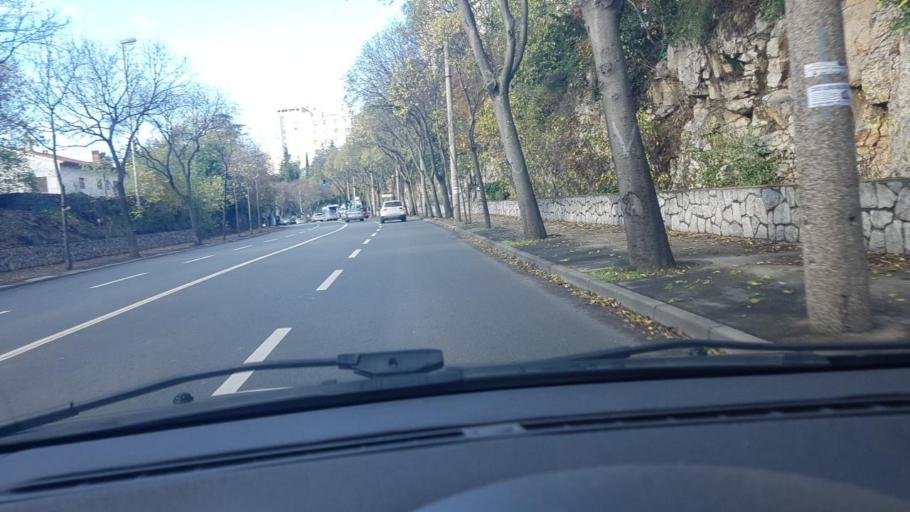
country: HR
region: Primorsko-Goranska
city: Rijeka
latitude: 45.3400
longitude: 14.3882
